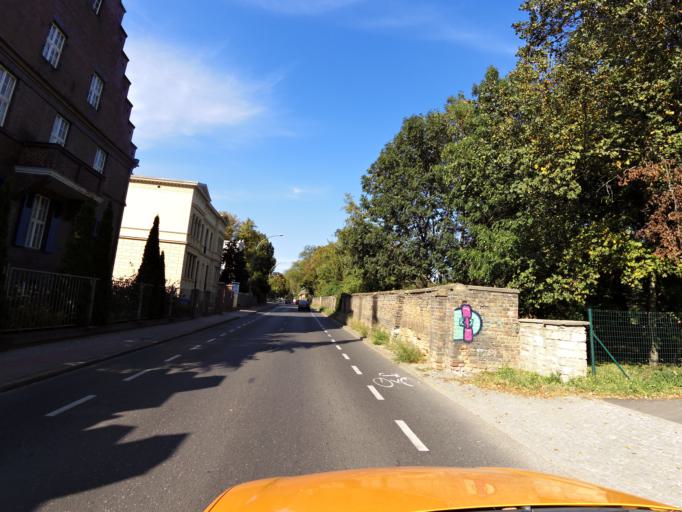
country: DE
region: Brandenburg
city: Potsdam
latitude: 52.4081
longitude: 13.0641
